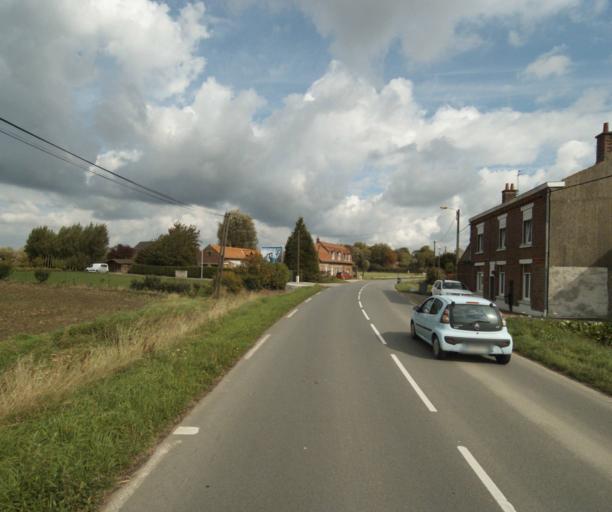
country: FR
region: Nord-Pas-de-Calais
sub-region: Departement du Nord
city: Perenchies
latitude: 50.6785
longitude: 2.9566
